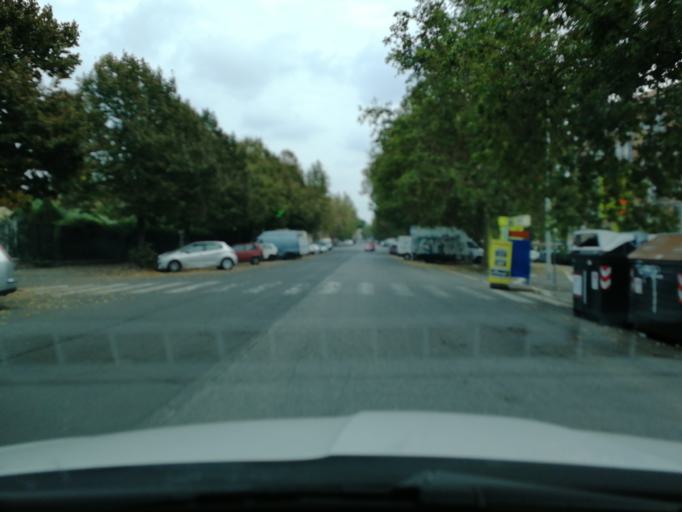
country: IT
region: Latium
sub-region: Citta metropolitana di Roma Capitale
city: Rome
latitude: 41.8595
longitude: 12.5524
